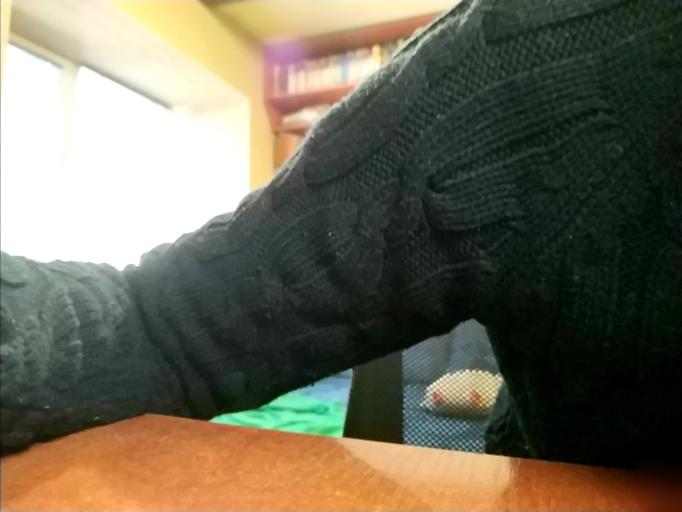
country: RU
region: Tverskaya
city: Sandovo
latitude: 58.6140
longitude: 36.4190
